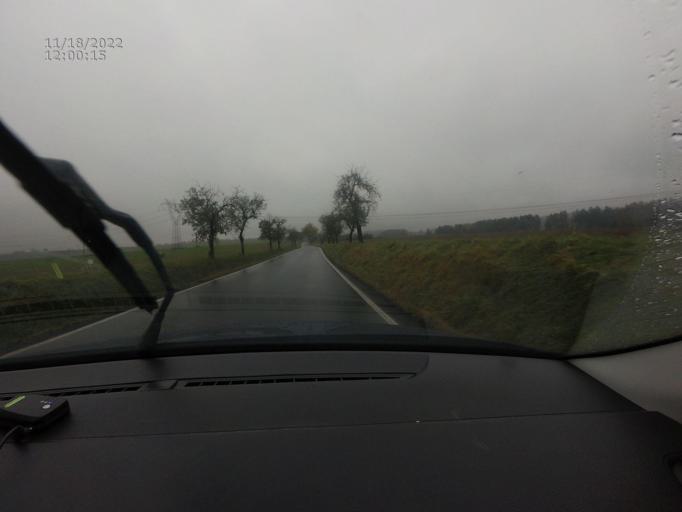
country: CZ
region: Plzensky
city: St'ahlavy
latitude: 49.6681
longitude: 13.4943
